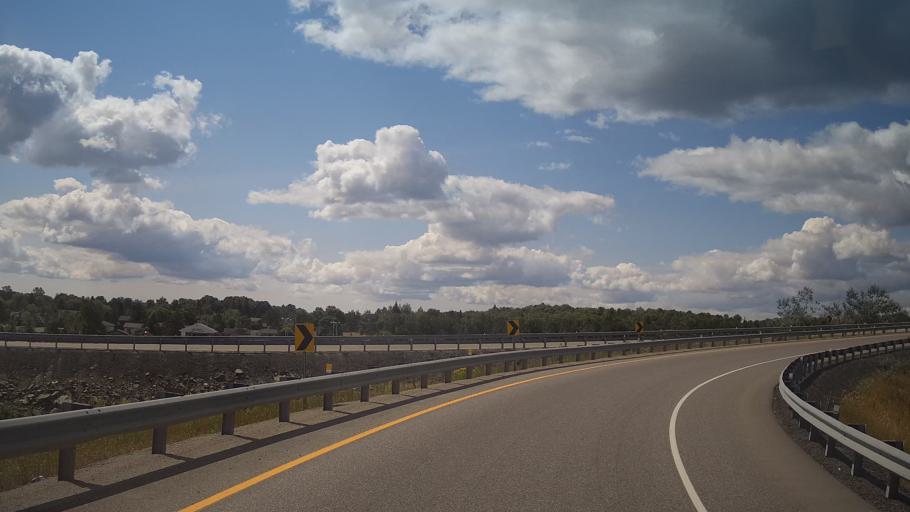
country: CA
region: Ontario
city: Greater Sudbury
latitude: 46.4264
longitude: -81.1202
